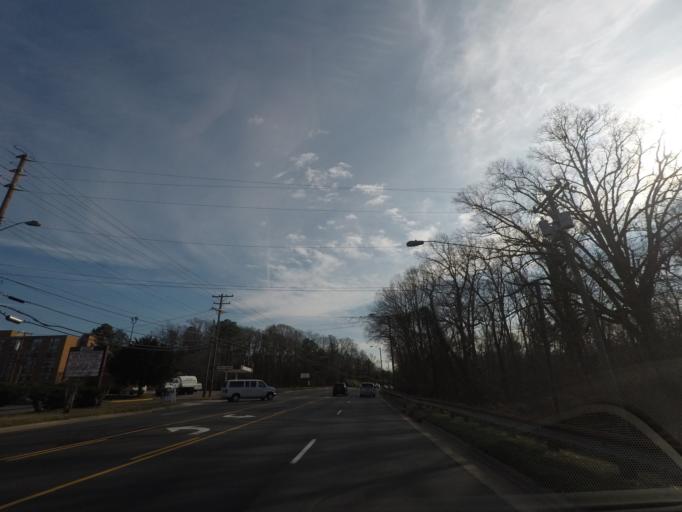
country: US
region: North Carolina
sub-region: Durham County
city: Durham
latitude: 36.0656
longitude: -78.9056
